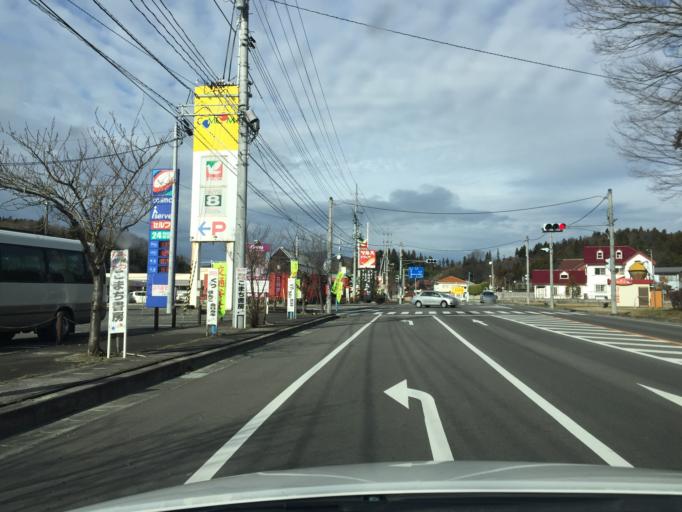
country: JP
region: Fukushima
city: Funehikimachi-funehiki
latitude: 37.3074
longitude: 140.6173
